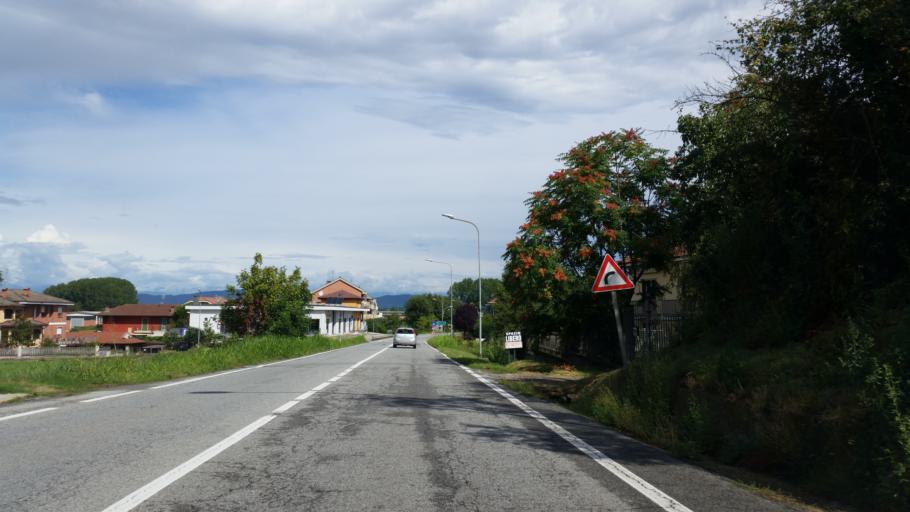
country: IT
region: Piedmont
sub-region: Provincia di Torino
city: Poirino
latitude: 44.9197
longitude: 7.8387
